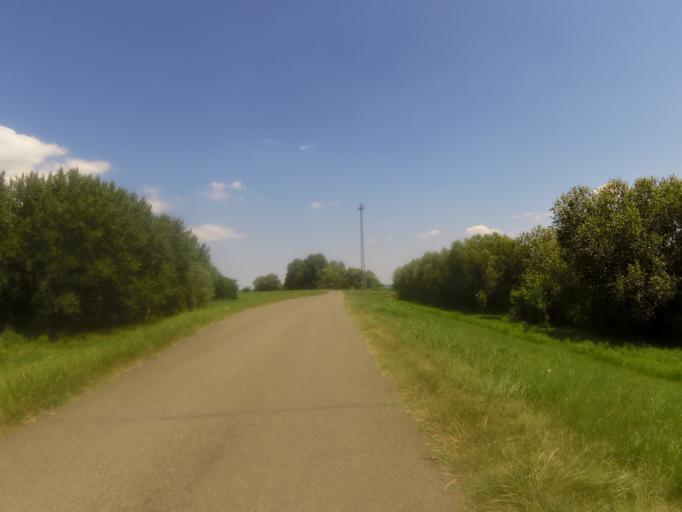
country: HU
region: Heves
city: Tiszanana
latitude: 47.5722
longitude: 20.6076
